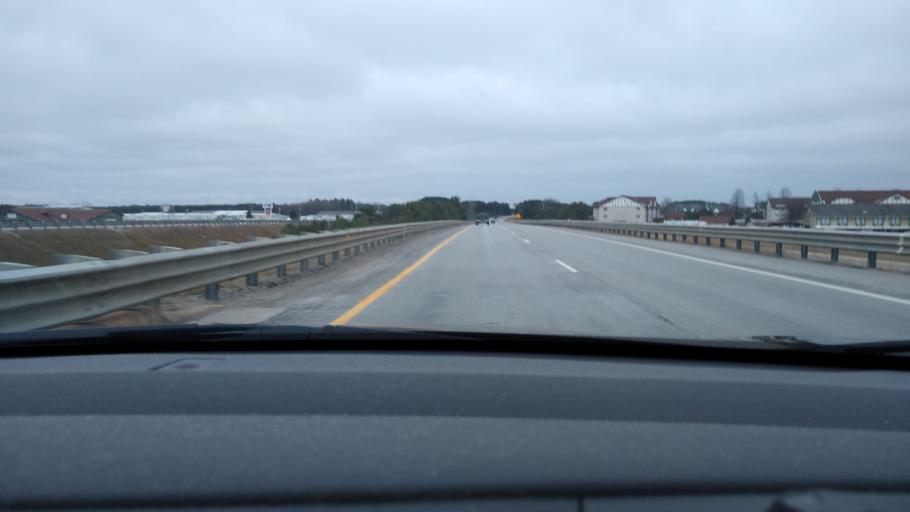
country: US
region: Michigan
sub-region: Otsego County
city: Gaylord
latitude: 45.0275
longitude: -84.6877
